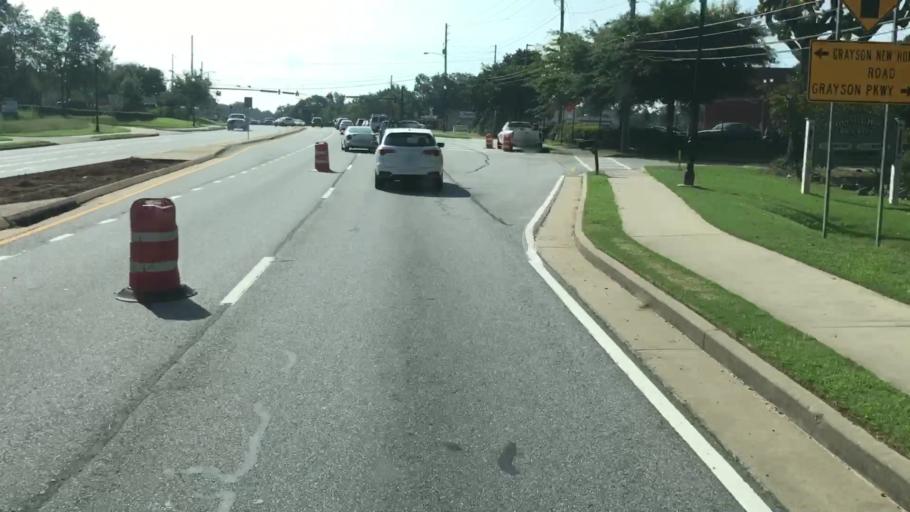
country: US
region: Georgia
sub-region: Gwinnett County
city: Grayson
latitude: 33.8952
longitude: -83.9573
